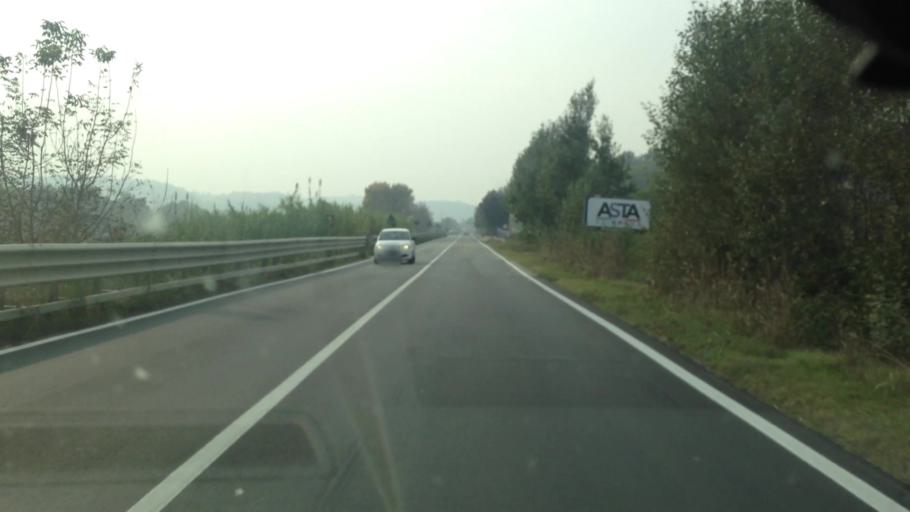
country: IT
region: Piedmont
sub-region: Provincia di Asti
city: Castello di Annone
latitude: 44.8787
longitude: 8.3311
